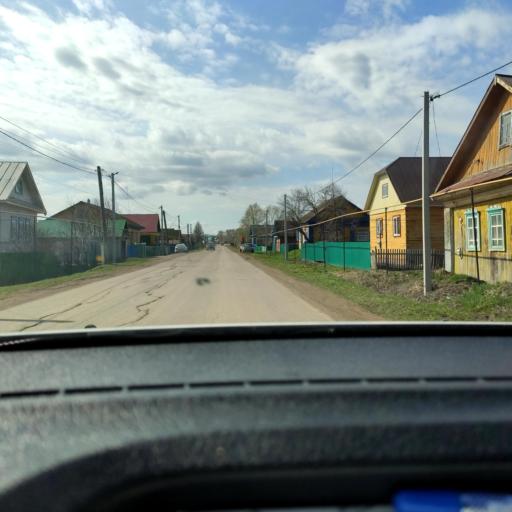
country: RU
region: Bashkortostan
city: Starobaltachevo
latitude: 55.9986
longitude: 55.9295
